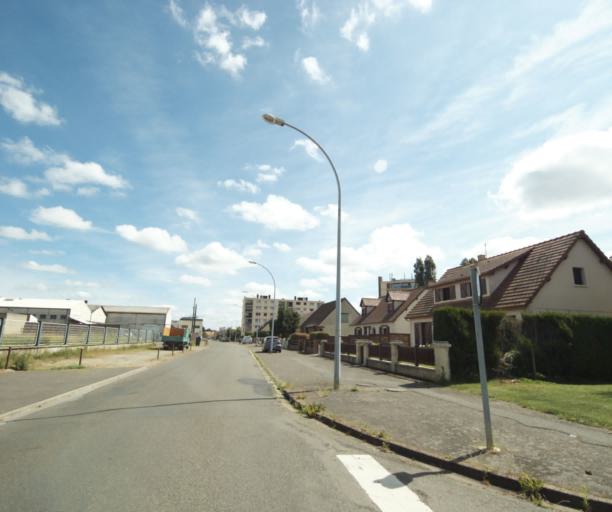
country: FR
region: Centre
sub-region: Departement d'Eure-et-Loir
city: Luisant
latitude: 48.4301
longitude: 1.4679
